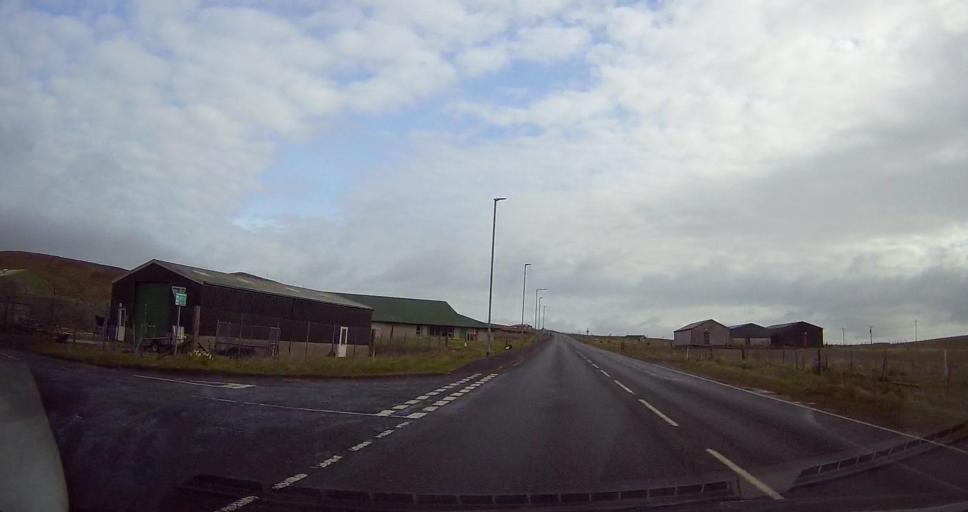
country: GB
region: Scotland
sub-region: Shetland Islands
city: Sandwick
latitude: 60.0564
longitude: -1.2252
